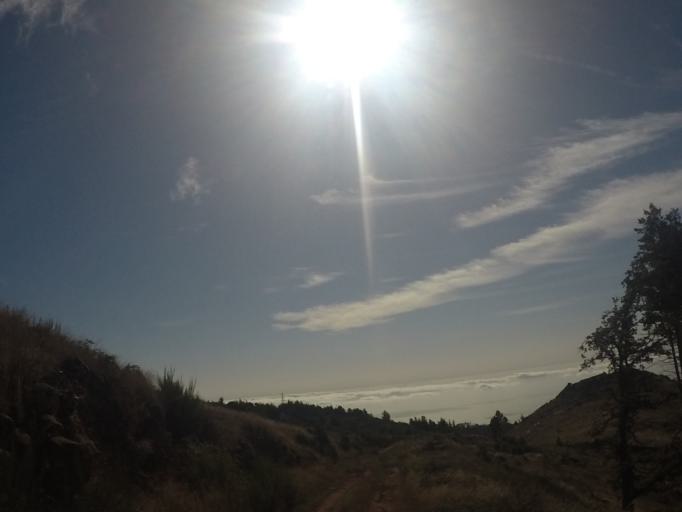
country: PT
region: Madeira
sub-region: Funchal
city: Nossa Senhora do Monte
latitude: 32.7036
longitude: -16.8994
